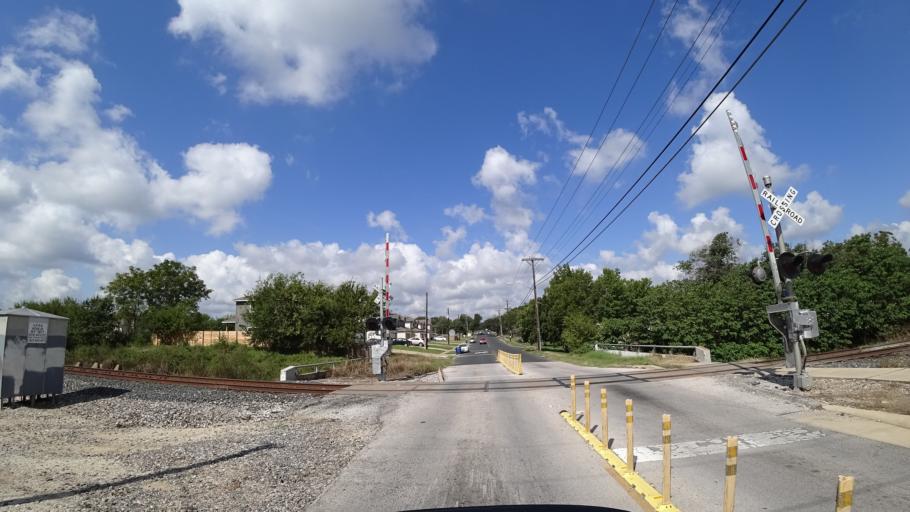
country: US
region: Texas
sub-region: Travis County
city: Manchaca
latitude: 30.1983
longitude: -97.8040
